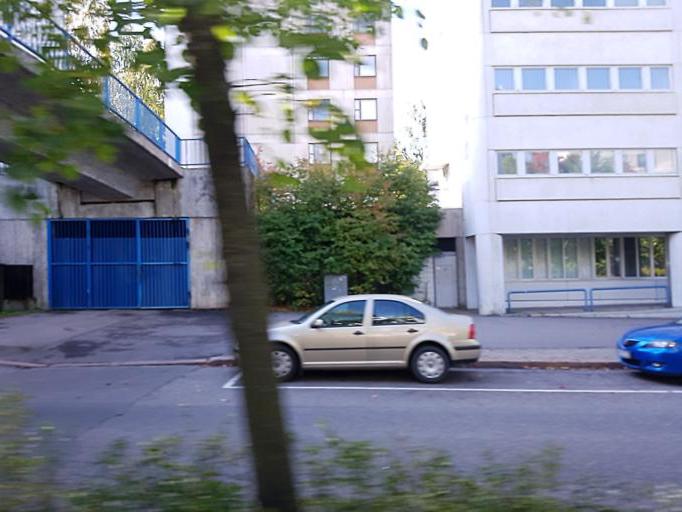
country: FI
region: Uusimaa
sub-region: Helsinki
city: Teekkarikylae
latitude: 60.2379
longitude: 24.8766
